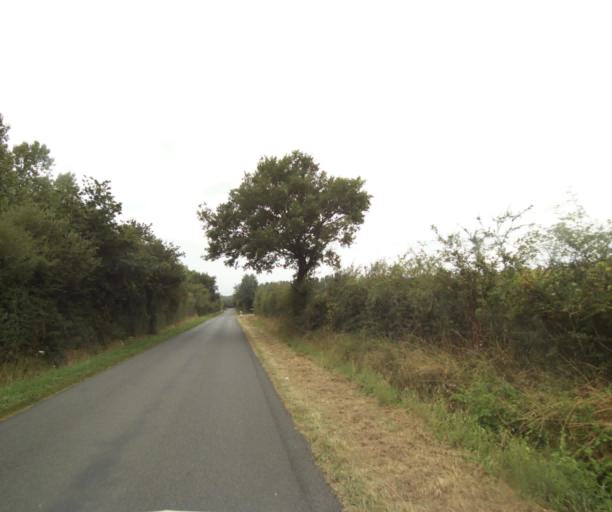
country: FR
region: Pays de la Loire
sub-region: Departement de la Sarthe
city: Solesmes
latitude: 47.8184
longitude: -0.2775
